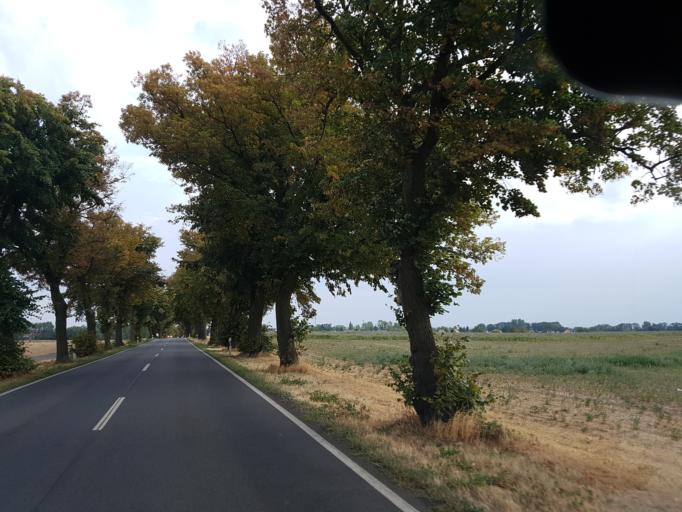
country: DE
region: Saxony-Anhalt
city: Wittenburg
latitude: 51.8860
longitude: 12.6267
